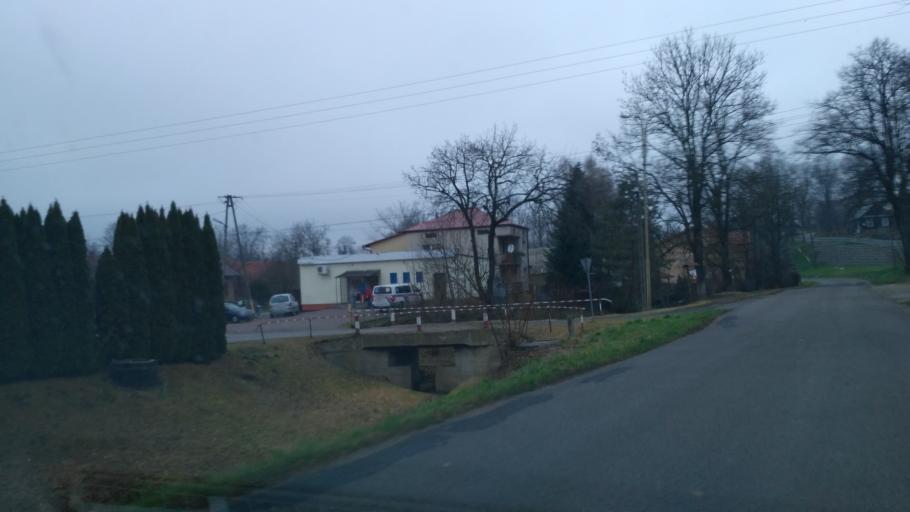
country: PL
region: Subcarpathian Voivodeship
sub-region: Powiat przeworski
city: Rozborz
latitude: 50.0566
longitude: 22.5456
